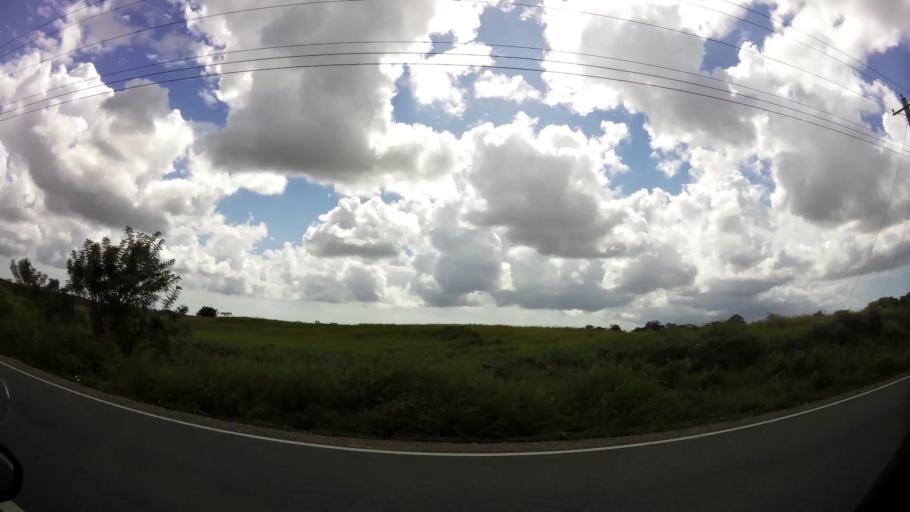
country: TT
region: Penal/Debe
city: Debe
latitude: 10.2221
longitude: -61.4783
